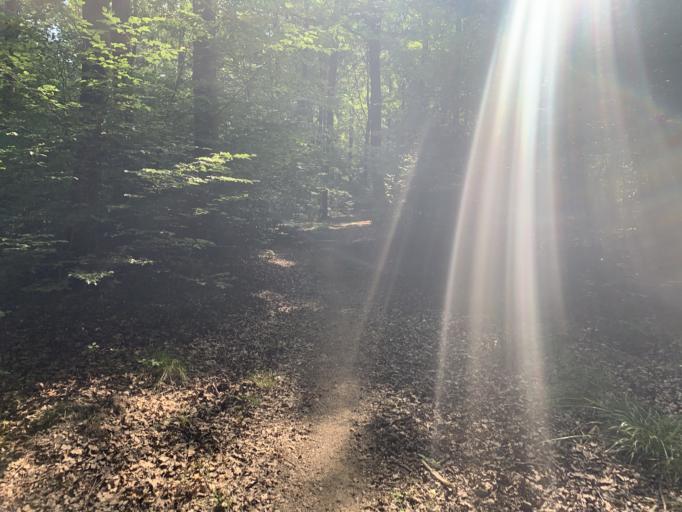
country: DE
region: Rheinland-Pfalz
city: Rettert
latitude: 50.2152
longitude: 7.9410
